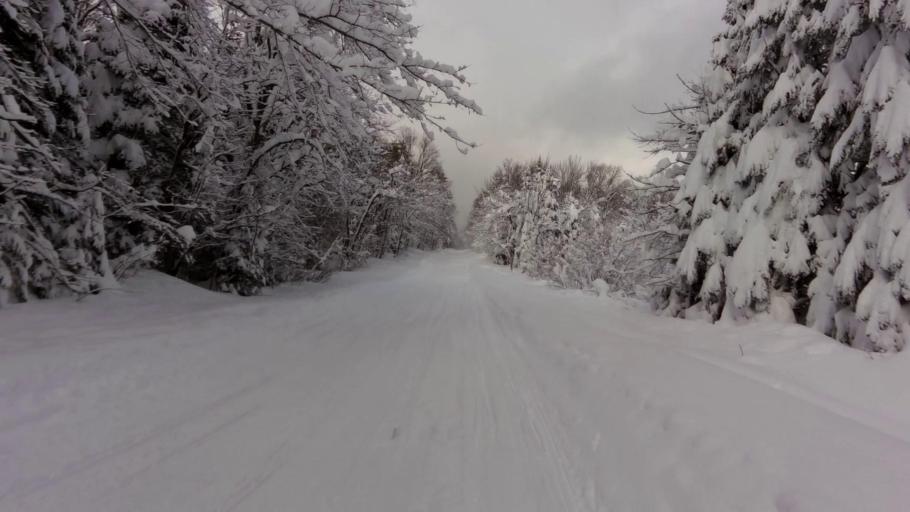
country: US
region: New York
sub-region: Lewis County
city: Lowville
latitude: 43.7480
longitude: -75.6751
